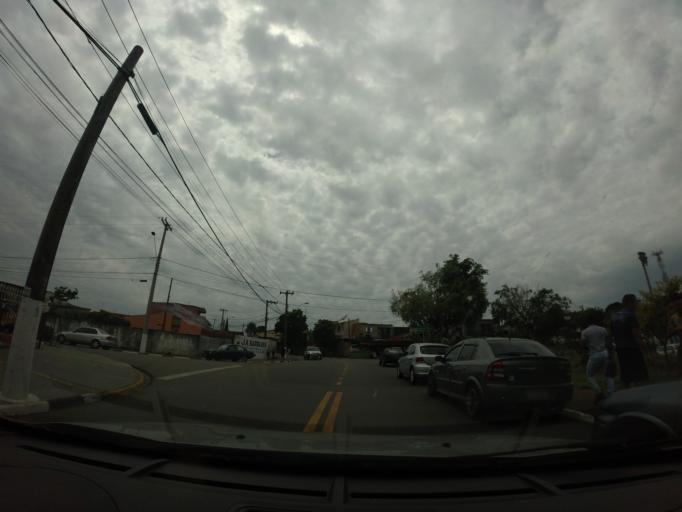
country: BR
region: Sao Paulo
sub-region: Hortolandia
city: Hortolandia
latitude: -22.8419
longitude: -47.1620
